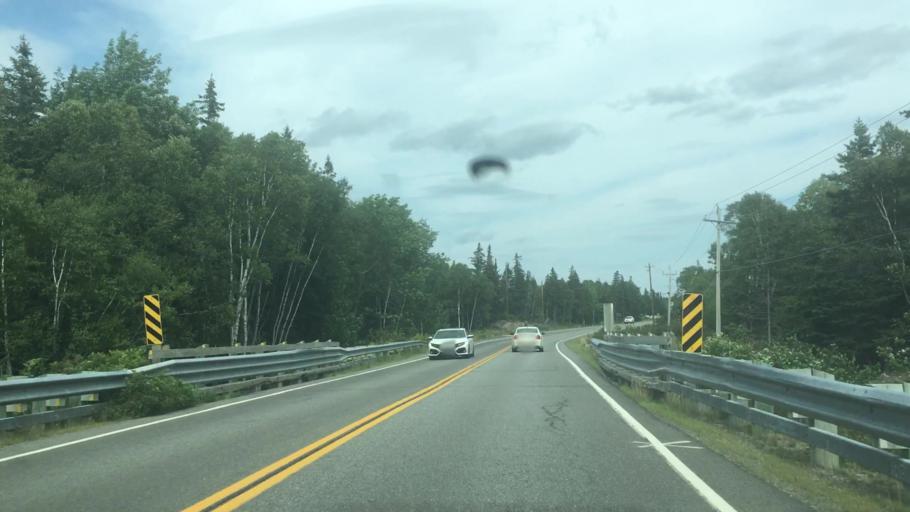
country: CA
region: Nova Scotia
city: Sydney Mines
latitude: 46.5132
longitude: -60.4297
